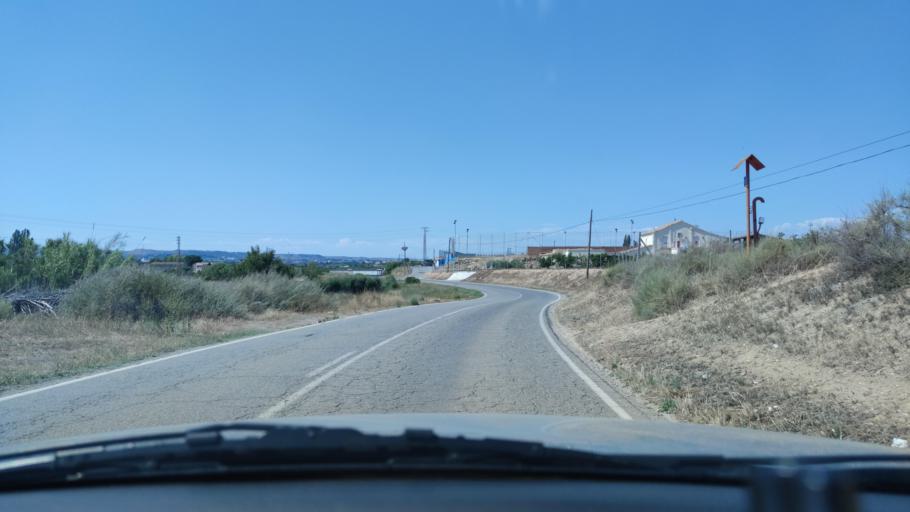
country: ES
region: Catalonia
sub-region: Provincia de Lleida
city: Lleida
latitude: 41.6408
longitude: 0.6251
